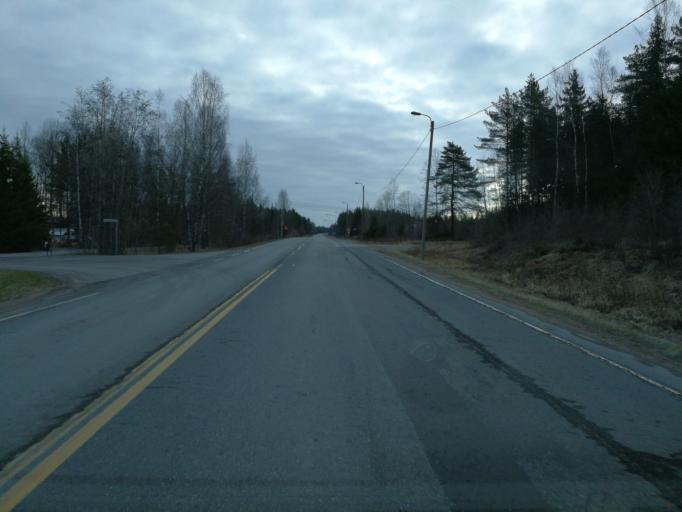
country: FI
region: Varsinais-Suomi
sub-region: Turku
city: Paimio
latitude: 60.4190
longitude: 22.6863
